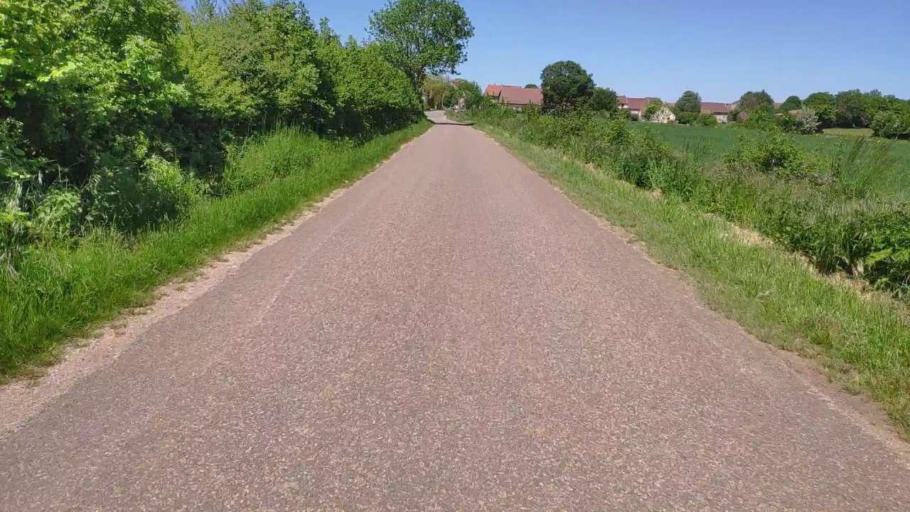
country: FR
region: Franche-Comte
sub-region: Departement du Jura
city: Poligny
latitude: 46.7332
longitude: 5.7050
